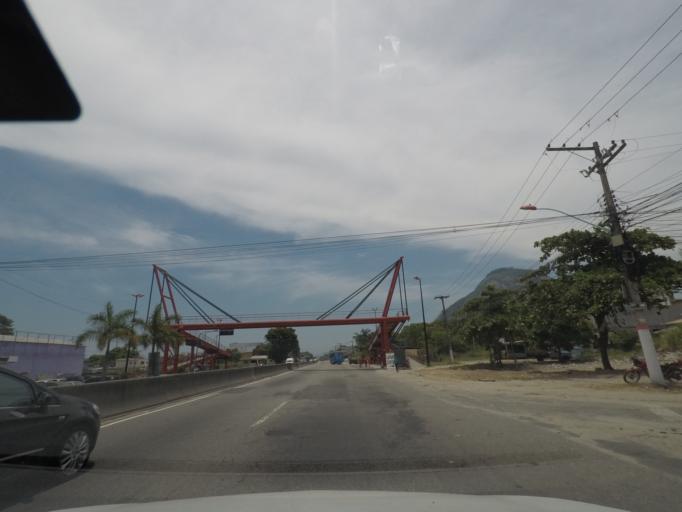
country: BR
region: Rio de Janeiro
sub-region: Marica
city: Marica
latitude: -22.9328
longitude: -42.8903
